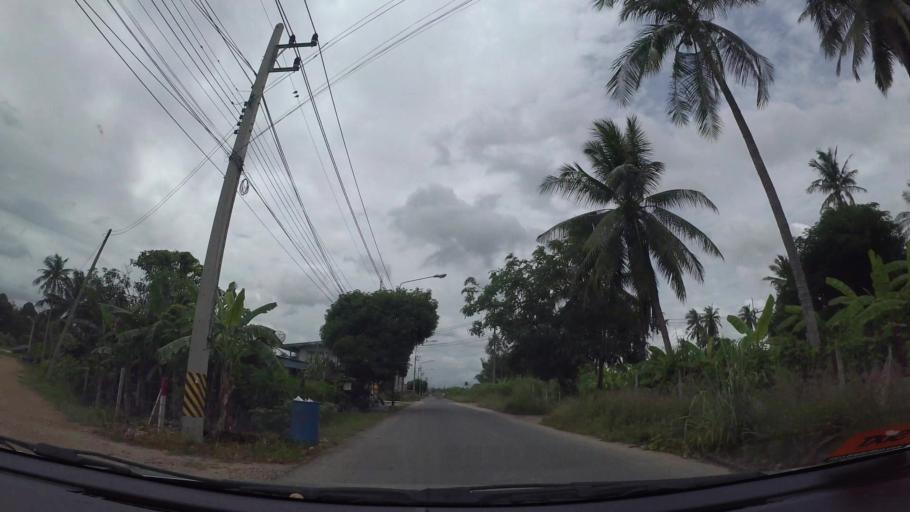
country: TH
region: Chon Buri
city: Si Racha
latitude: 13.1851
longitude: 100.9876
